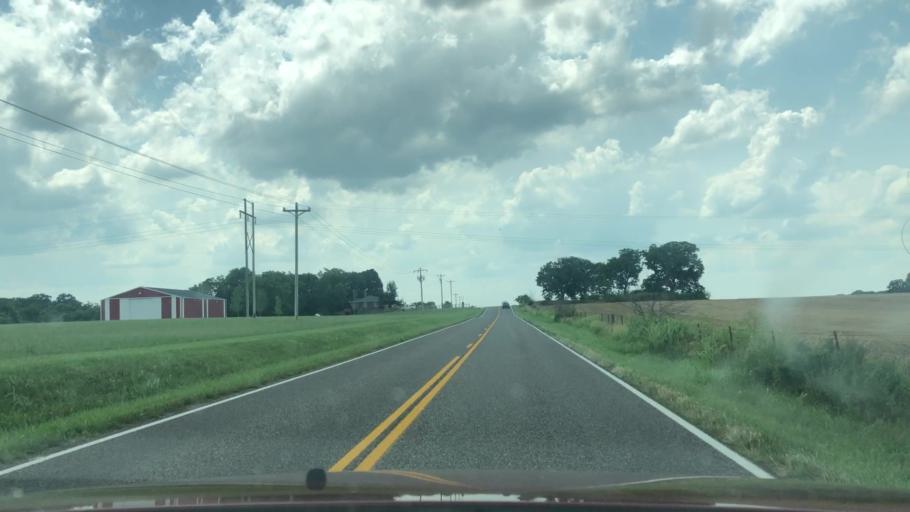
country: US
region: Missouri
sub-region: Christian County
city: Ozark
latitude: 36.9431
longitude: -93.2431
